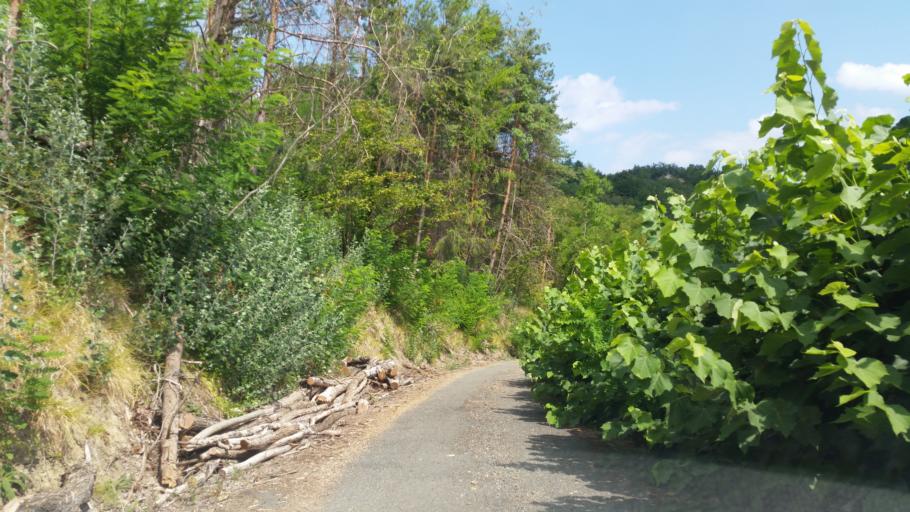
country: IT
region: Piedmont
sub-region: Provincia di Asti
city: Bubbio
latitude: 44.6313
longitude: 8.2893
